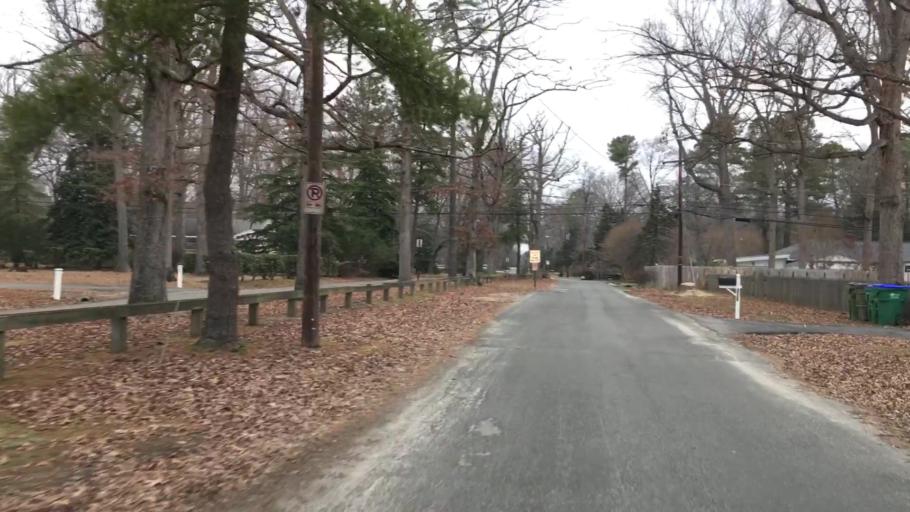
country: US
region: Virginia
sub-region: Chesterfield County
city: Bon Air
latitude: 37.5336
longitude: -77.5737
